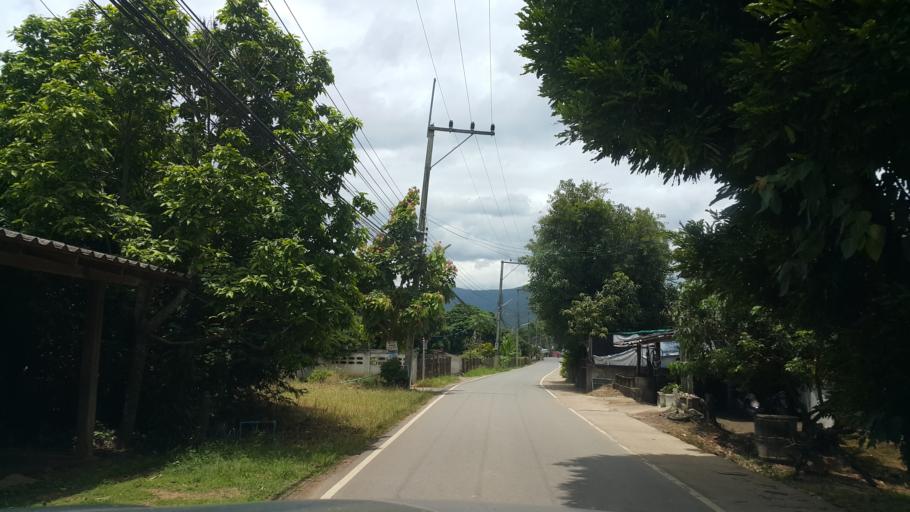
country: TH
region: Chiang Mai
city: Mae Taeng
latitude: 19.1877
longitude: 98.9947
